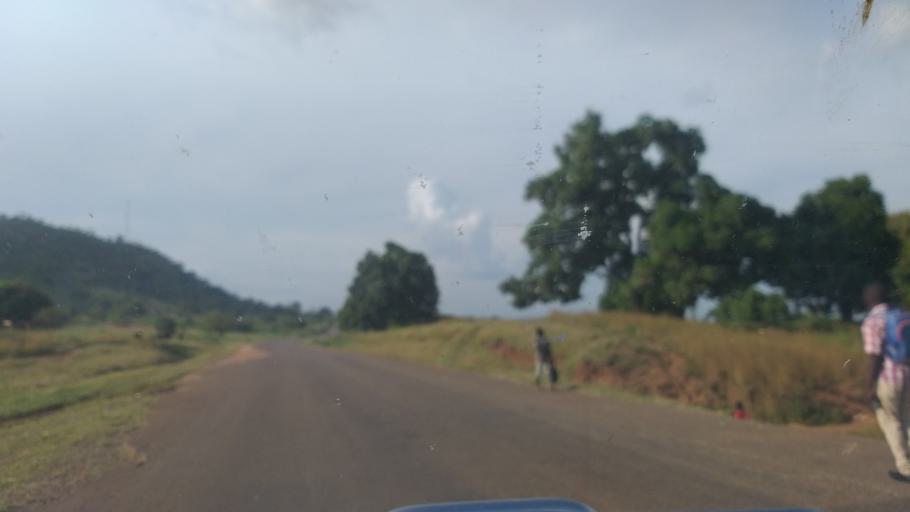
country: UG
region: Northern Region
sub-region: Arua District
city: Arua
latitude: 2.8301
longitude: 30.9950
